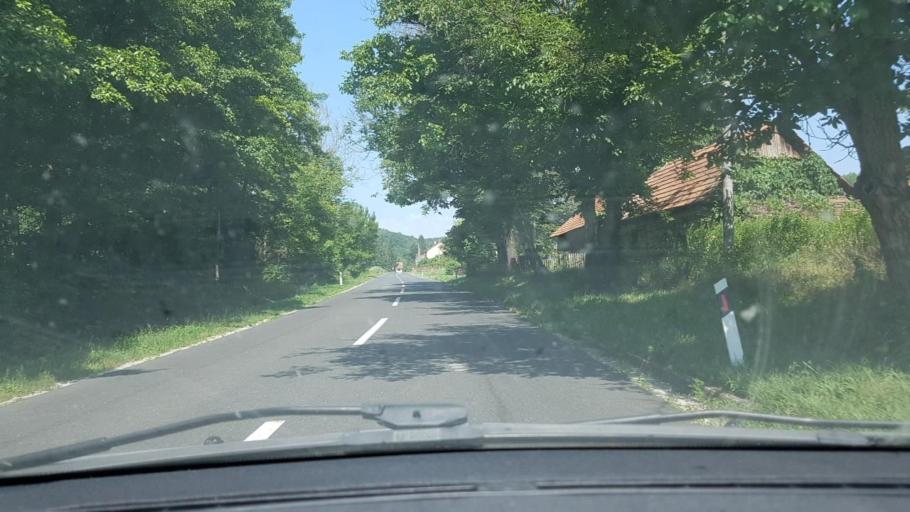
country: HR
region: Karlovacka
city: Vojnic
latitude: 45.2413
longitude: 15.7337
